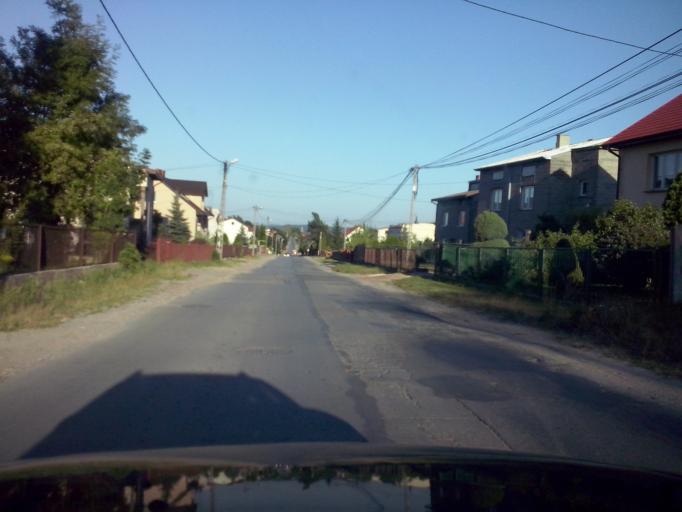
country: PL
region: Swietokrzyskie
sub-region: Powiat kielecki
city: Kielce
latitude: 50.8183
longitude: 20.6328
